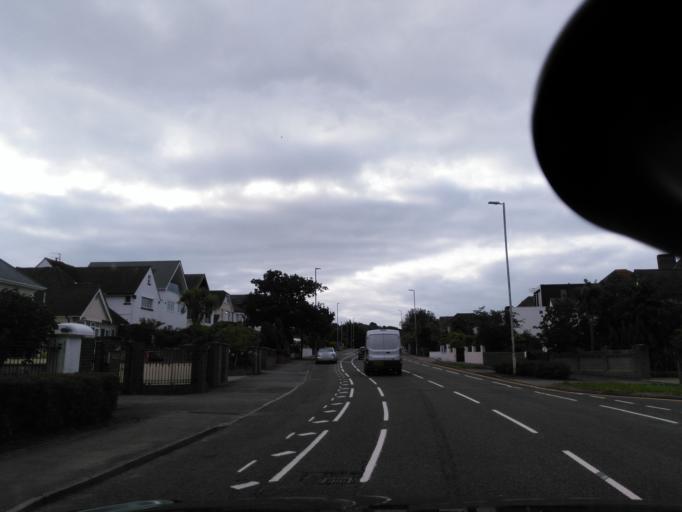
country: GB
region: England
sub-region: Dorset
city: Parkstone
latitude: 50.7117
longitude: -1.9490
